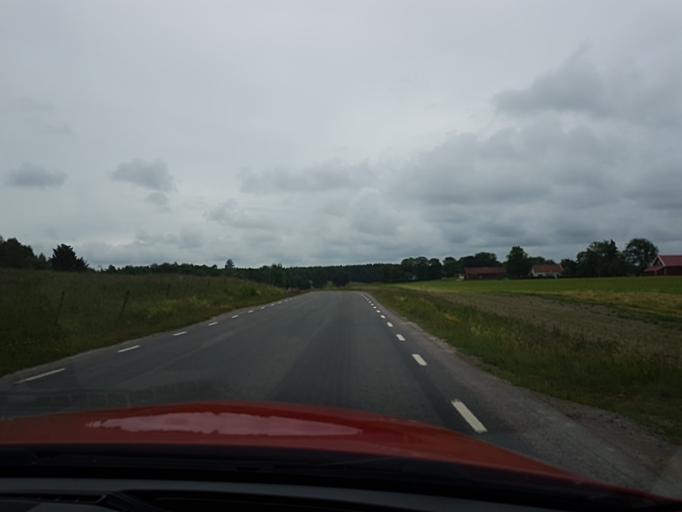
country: SE
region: Vaestra Goetaland
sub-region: Skovde Kommun
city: Skoevde
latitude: 58.3646
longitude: 13.9465
